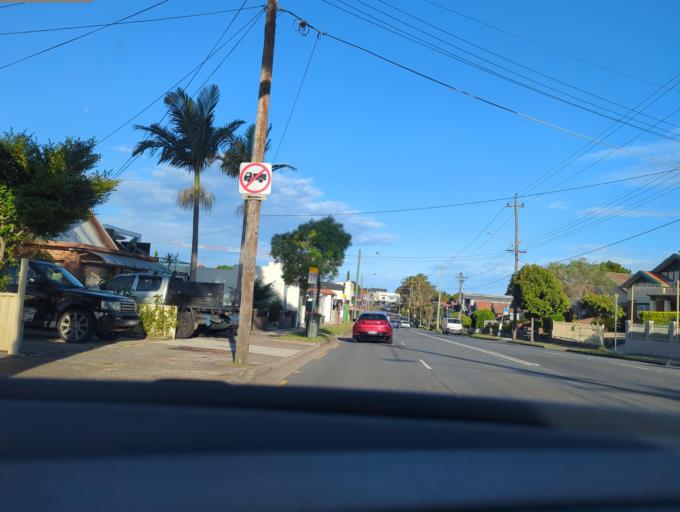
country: AU
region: New South Wales
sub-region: Rockdale
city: Bexley
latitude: -33.9497
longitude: 151.1222
